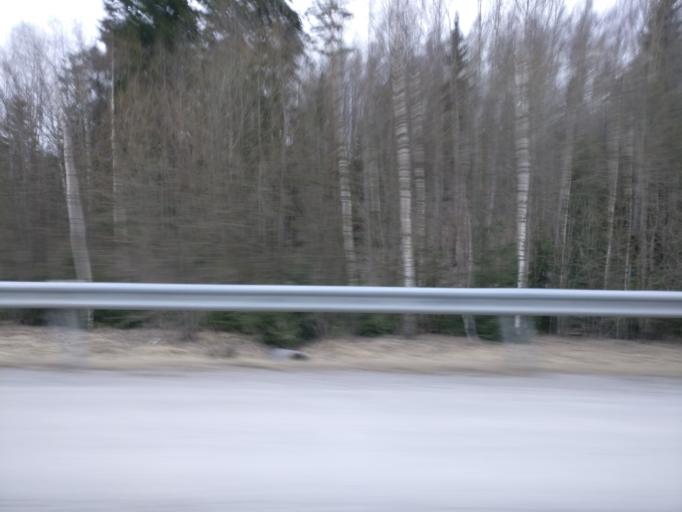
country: FI
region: Uusimaa
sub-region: Helsinki
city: Nurmijaervi
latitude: 60.3826
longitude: 24.8148
